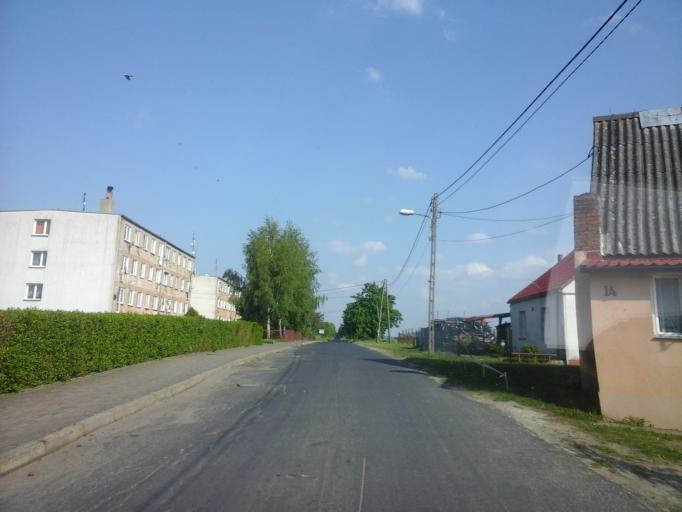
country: PL
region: West Pomeranian Voivodeship
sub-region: Powiat choszczenski
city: Pelczyce
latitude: 53.0830
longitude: 15.3580
